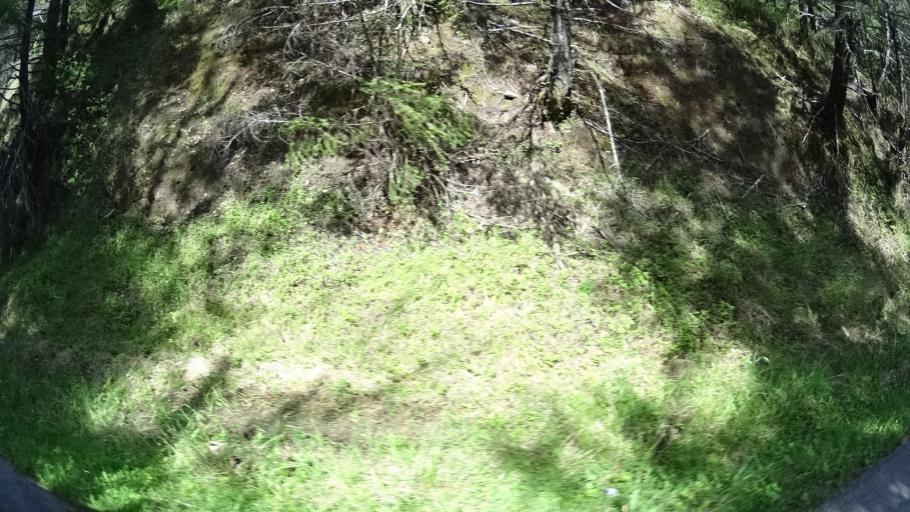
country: US
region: California
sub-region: Humboldt County
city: Redway
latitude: 40.4352
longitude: -123.7757
